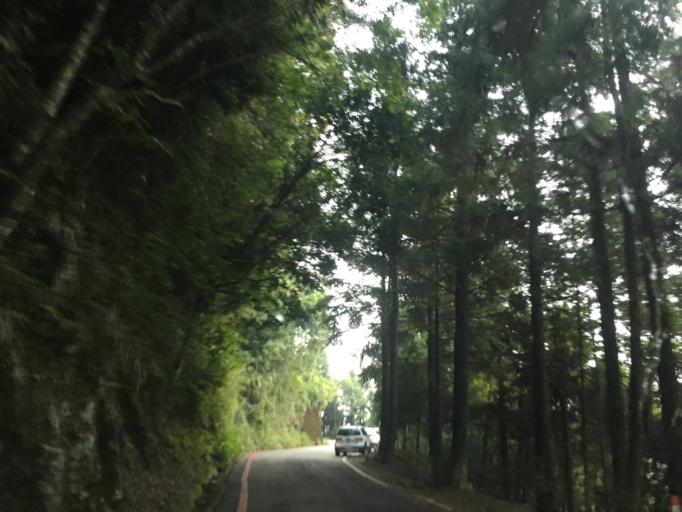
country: TW
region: Taiwan
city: Fengyuan
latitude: 24.2360
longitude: 120.9569
